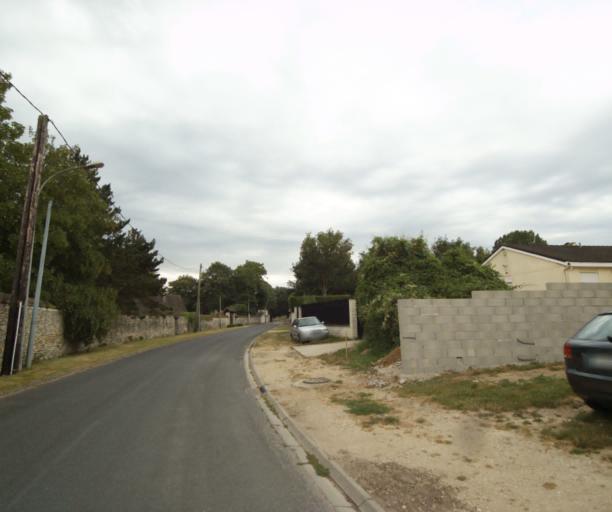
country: FR
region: Ile-de-France
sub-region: Departement de Seine-et-Marne
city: Cely
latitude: 48.4663
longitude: 2.5212
